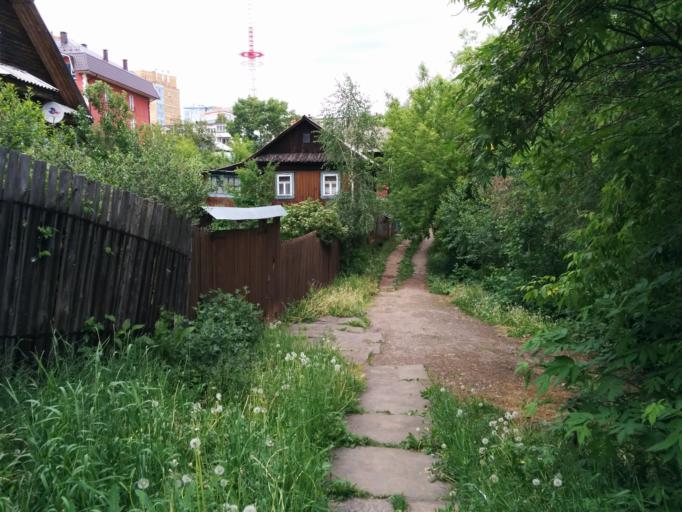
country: RU
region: Perm
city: Perm
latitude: 58.0203
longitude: 56.2648
